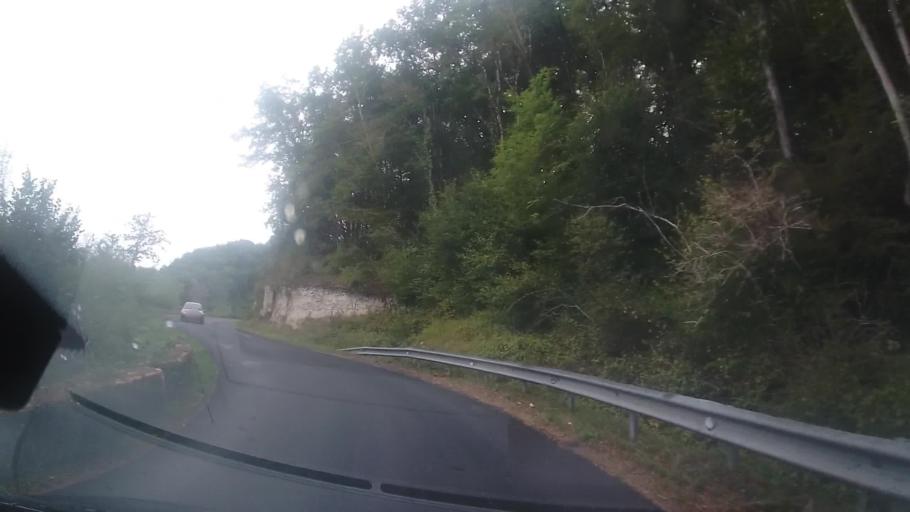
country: FR
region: Aquitaine
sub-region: Departement de la Dordogne
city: Cenac-et-Saint-Julien
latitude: 44.7980
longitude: 1.1911
